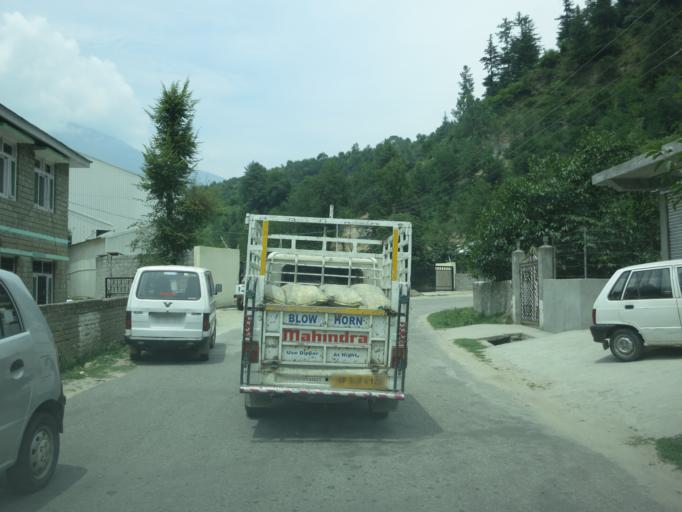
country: IN
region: Himachal Pradesh
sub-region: Kulu
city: Nagar
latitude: 32.1098
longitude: 77.1518
